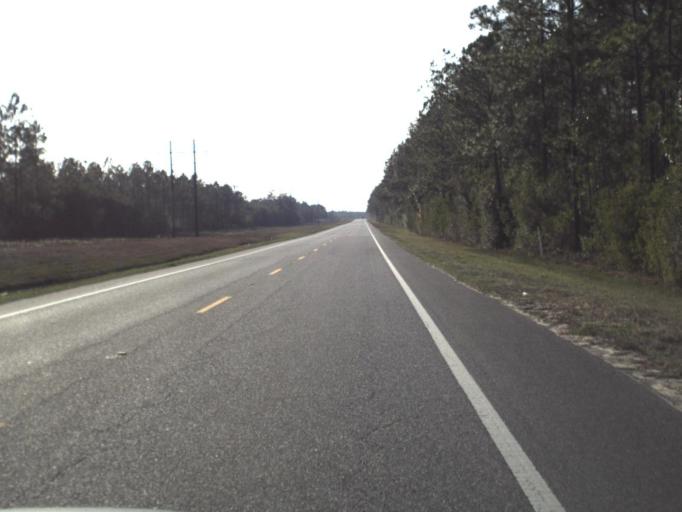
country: US
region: Florida
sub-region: Bay County
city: Laguna Beach
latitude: 30.4399
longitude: -85.7944
